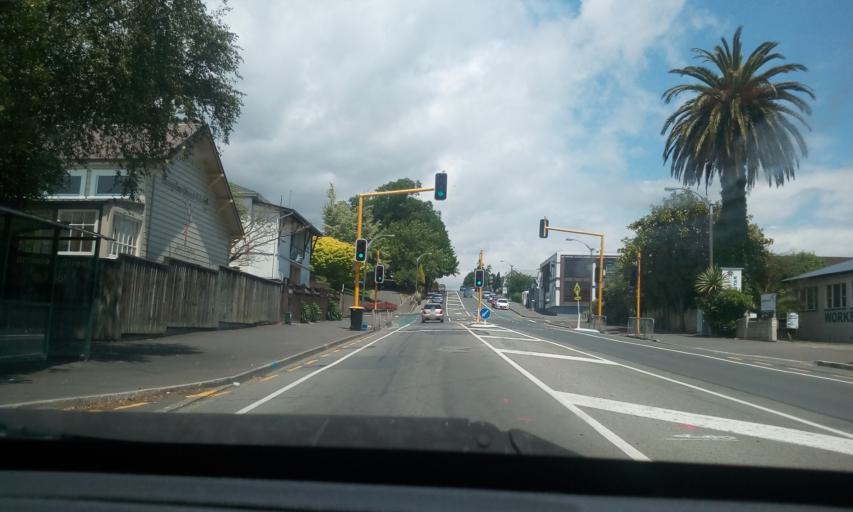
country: NZ
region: Nelson
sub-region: Nelson City
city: Nelson
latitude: -41.2837
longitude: 173.2771
